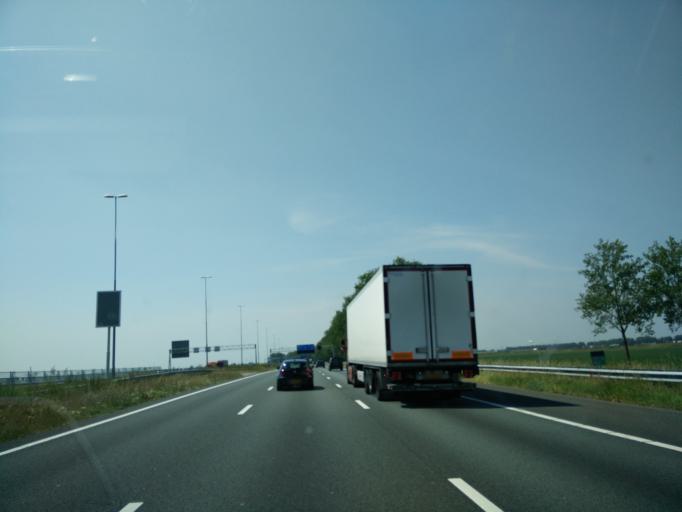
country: NL
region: South Holland
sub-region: Gemeente Kaag en Braassem
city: Oude Wetering
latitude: 52.2270
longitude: 4.6392
